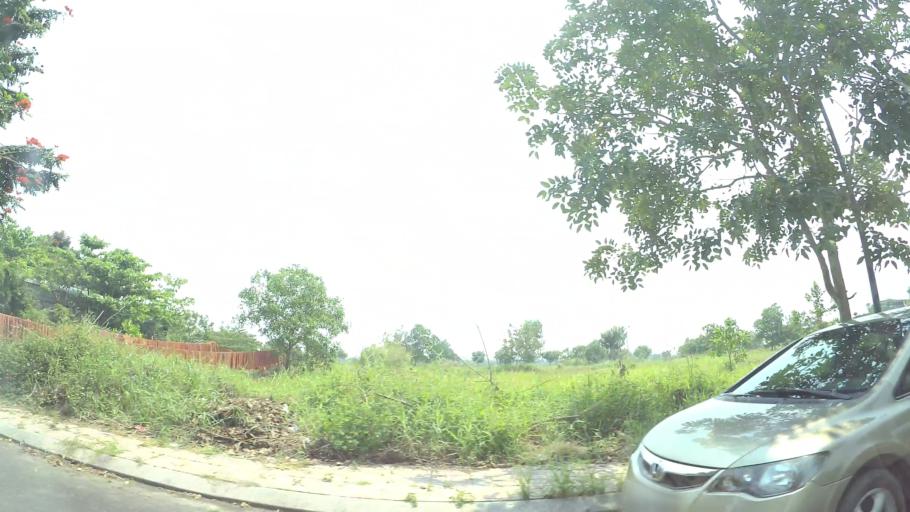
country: VN
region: Da Nang
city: Cam Le
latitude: 16.0142
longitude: 108.2100
